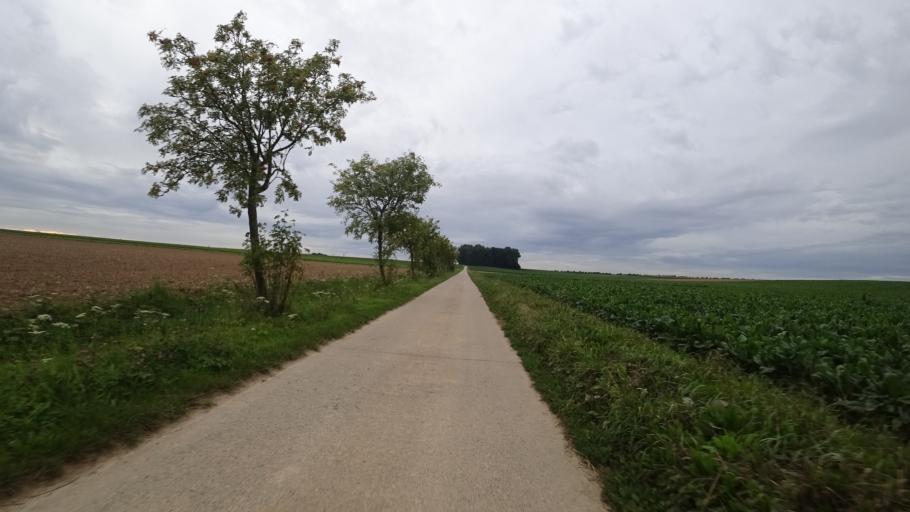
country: BE
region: Wallonia
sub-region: Province du Brabant Wallon
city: Walhain-Saint-Paul
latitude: 50.6250
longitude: 4.6773
